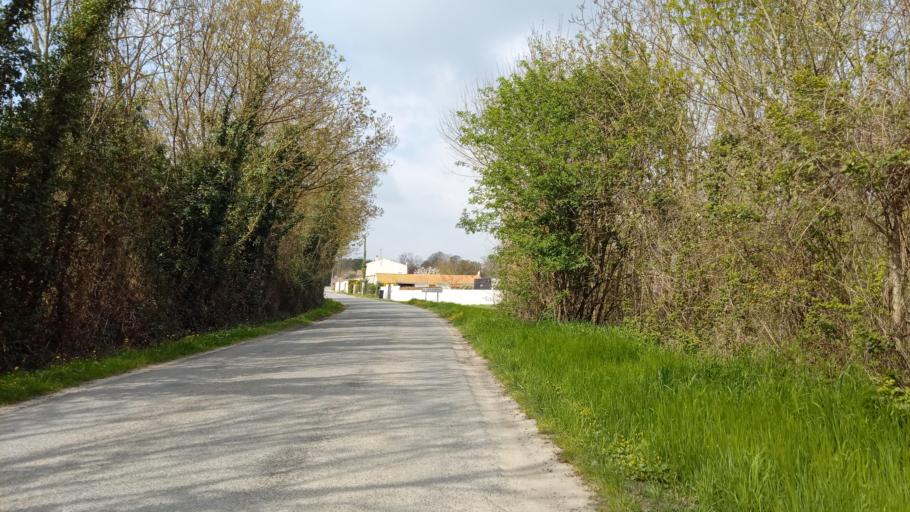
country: FR
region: Poitou-Charentes
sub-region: Departement de la Charente-Maritime
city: Verines
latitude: 46.1481
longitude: -0.9393
